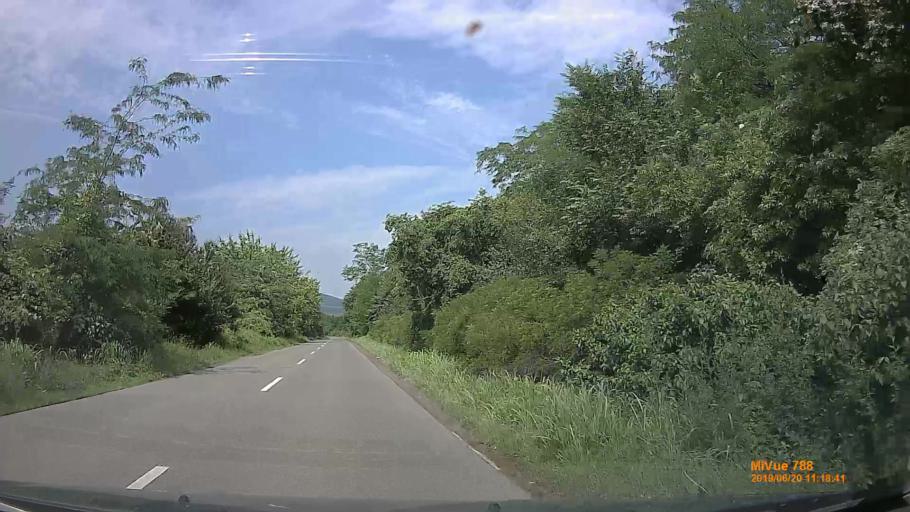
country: HU
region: Baranya
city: Pecsvarad
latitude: 46.1679
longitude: 18.4574
